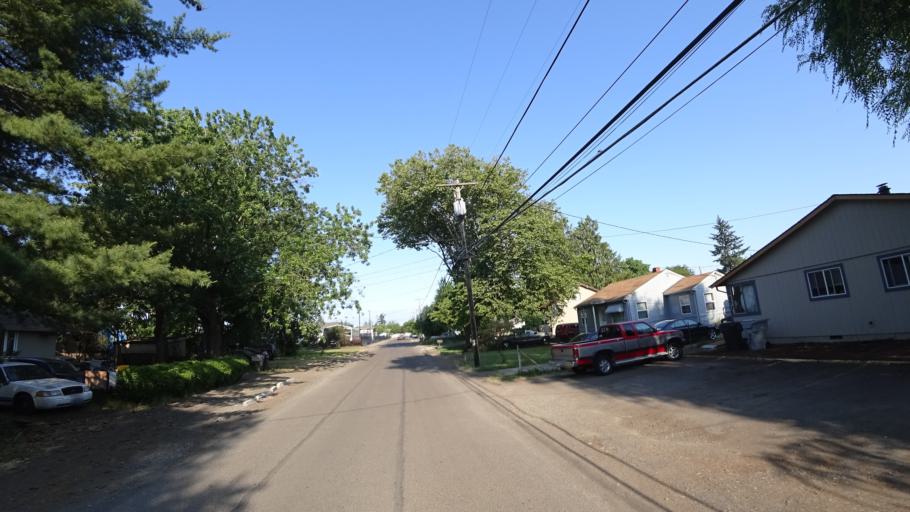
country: US
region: Oregon
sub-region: Multnomah County
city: Lents
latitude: 45.4576
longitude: -122.5761
